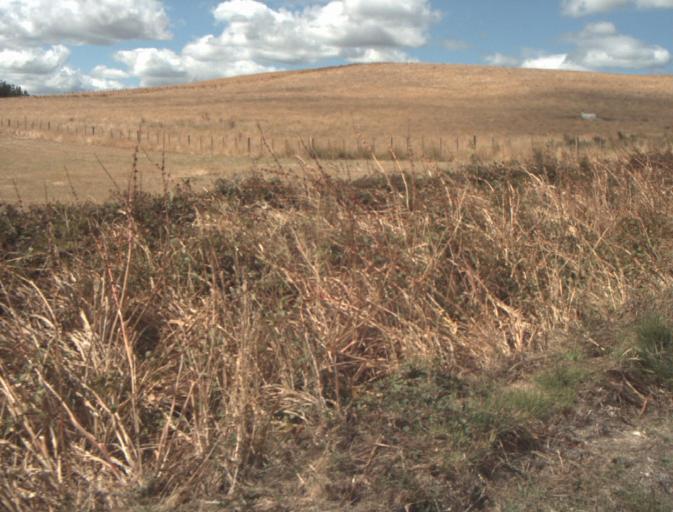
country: AU
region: Tasmania
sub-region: Launceston
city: Mayfield
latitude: -41.2132
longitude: 147.1082
